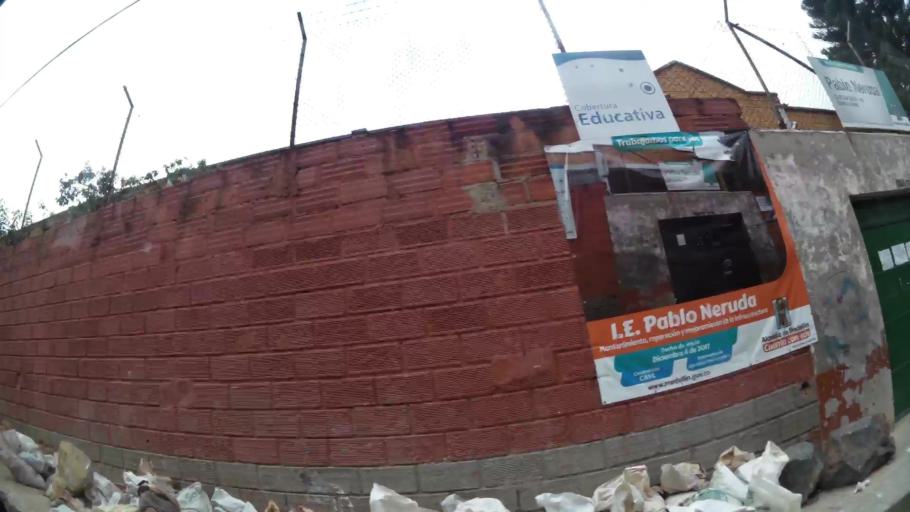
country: CO
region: Antioquia
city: Medellin
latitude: 6.2908
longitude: -75.5598
